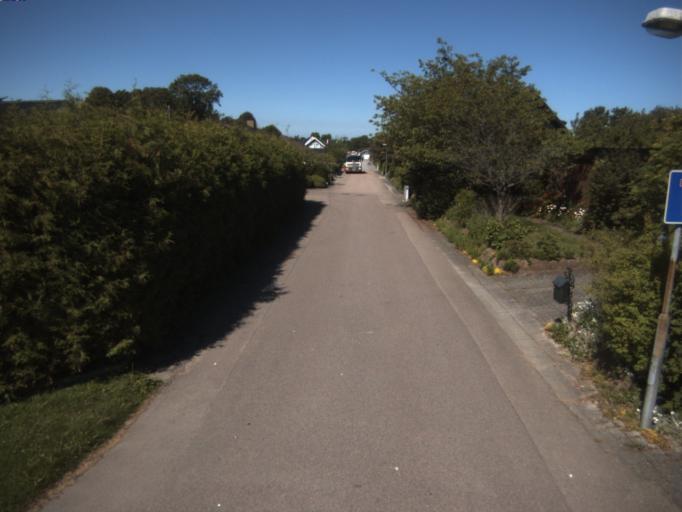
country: SE
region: Skane
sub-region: Helsingborg
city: Barslov
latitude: 56.0062
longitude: 12.8204
